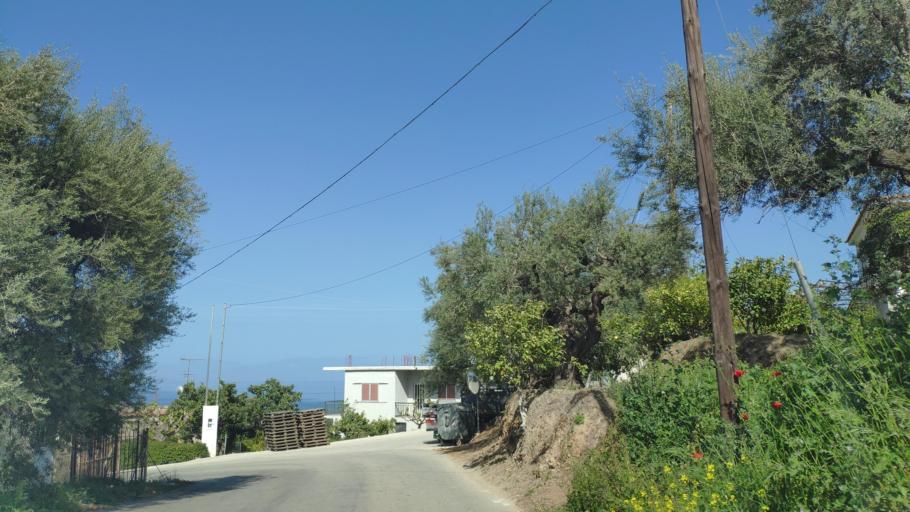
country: GR
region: West Greece
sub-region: Nomos Achaias
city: Aiyira
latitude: 38.1420
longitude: 22.3510
